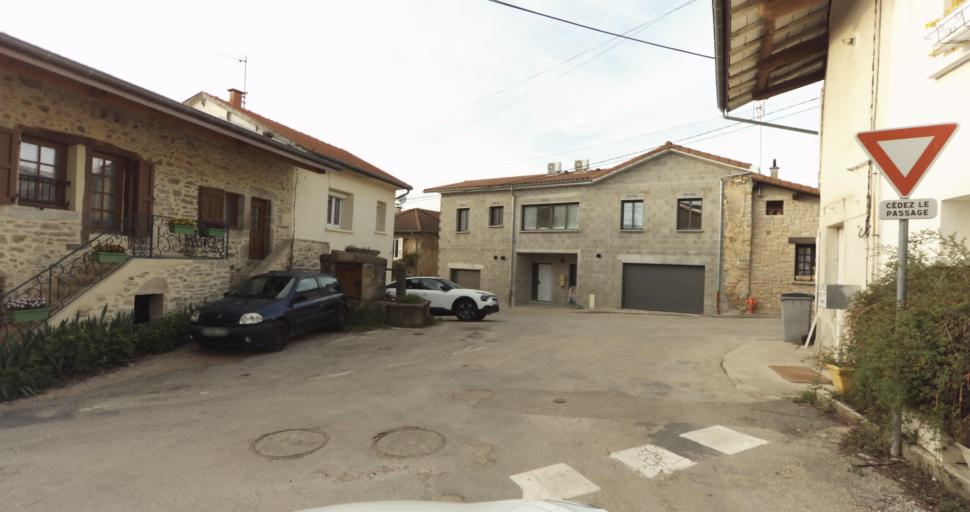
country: FR
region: Rhone-Alpes
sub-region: Departement de l'Ain
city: Amberieu-en-Bugey
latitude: 45.9657
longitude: 5.3629
